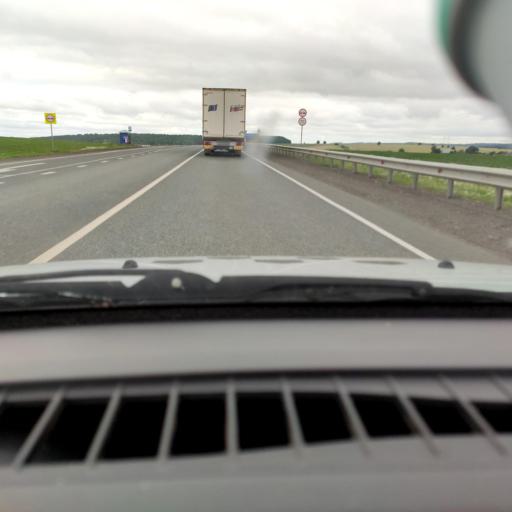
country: RU
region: Udmurtiya
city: Alnashi
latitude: 56.1151
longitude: 52.4612
